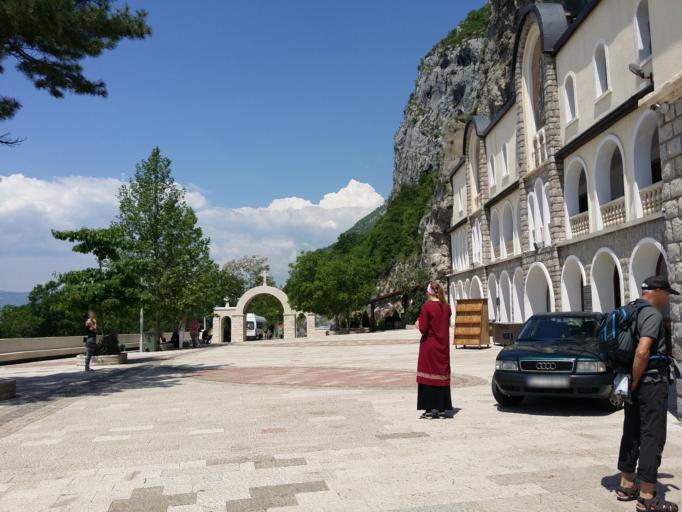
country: ME
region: Opstina Niksic
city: Niksic
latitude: 42.6747
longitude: 19.0306
